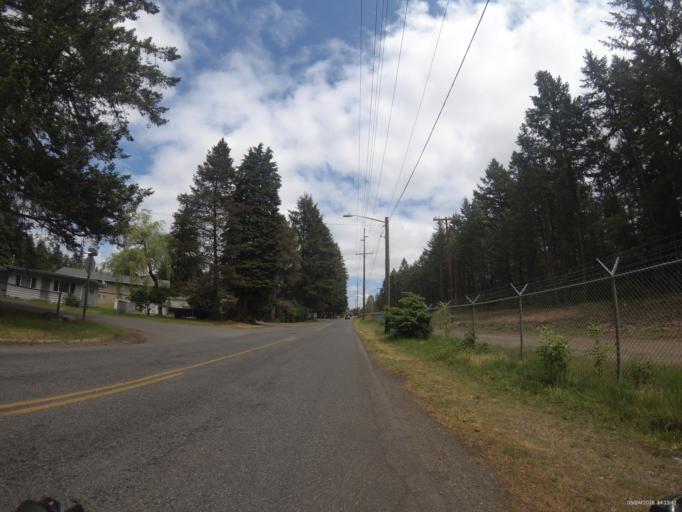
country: US
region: Washington
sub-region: Pierce County
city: McChord Air Force Base
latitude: 47.1393
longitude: -122.5078
